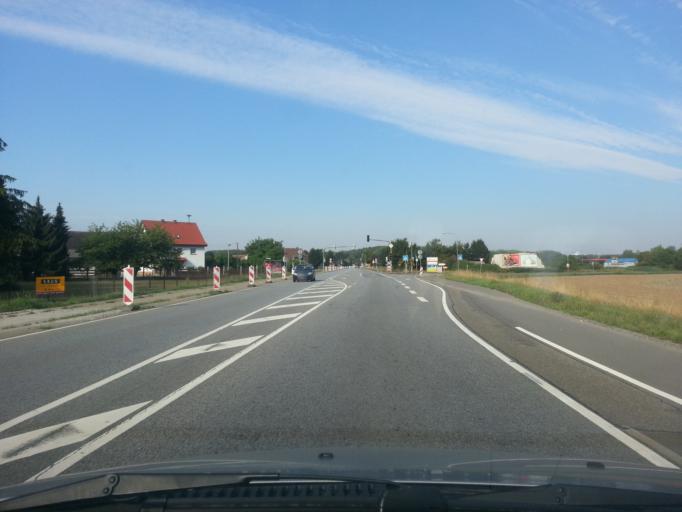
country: DE
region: Rheinland-Pfalz
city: Worms
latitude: 49.6360
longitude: 8.4037
